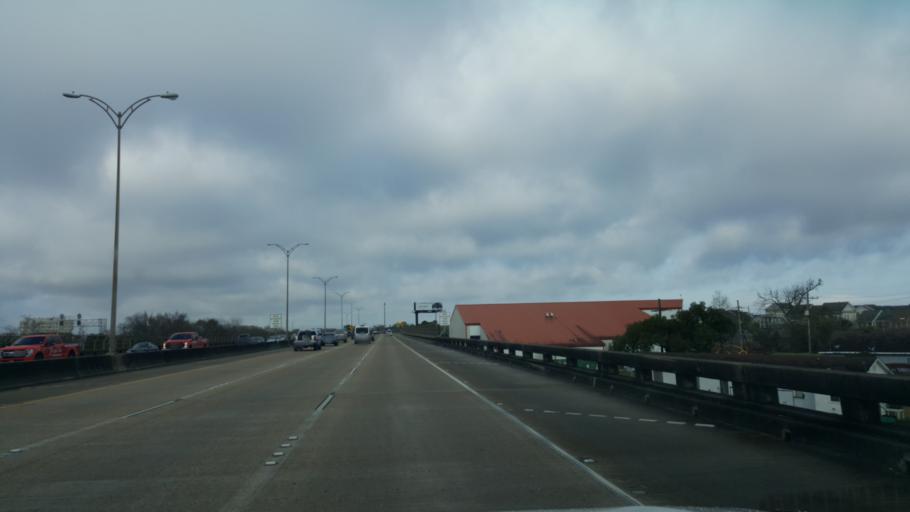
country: US
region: Louisiana
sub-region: Orleans Parish
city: New Orleans
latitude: 29.9917
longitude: -90.0735
